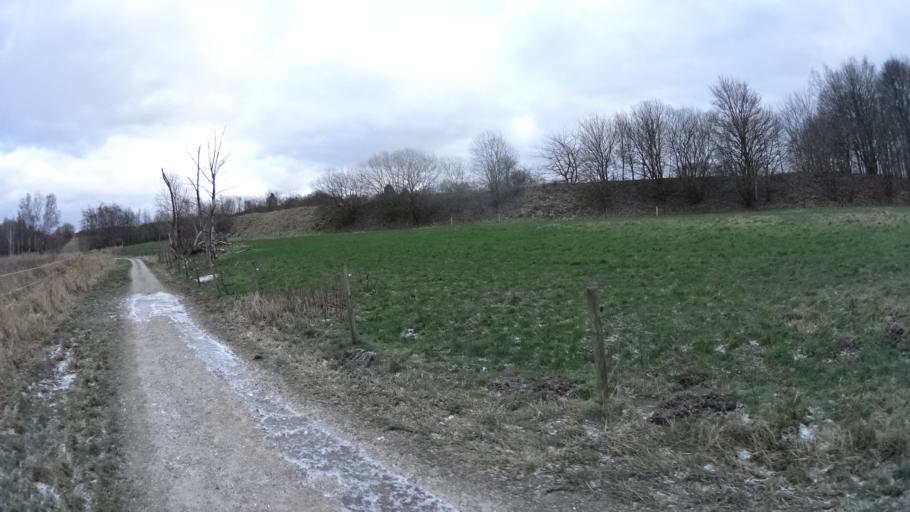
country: DK
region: Central Jutland
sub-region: Arhus Kommune
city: Kolt
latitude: 56.1240
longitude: 10.0614
